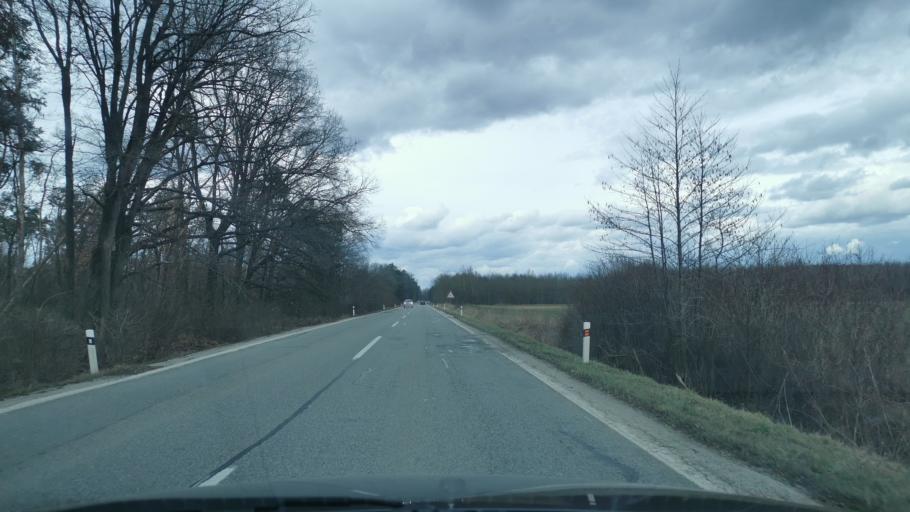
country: SK
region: Trnavsky
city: Gbely
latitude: 48.7591
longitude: 17.0806
